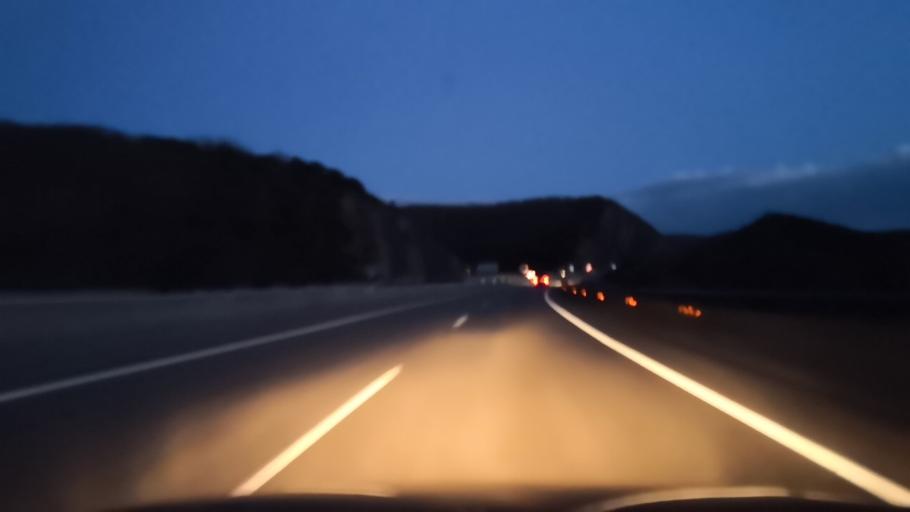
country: ES
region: Castille and Leon
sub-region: Provincia de Leon
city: Folgoso de la Ribera
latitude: 42.6203
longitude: -6.2814
